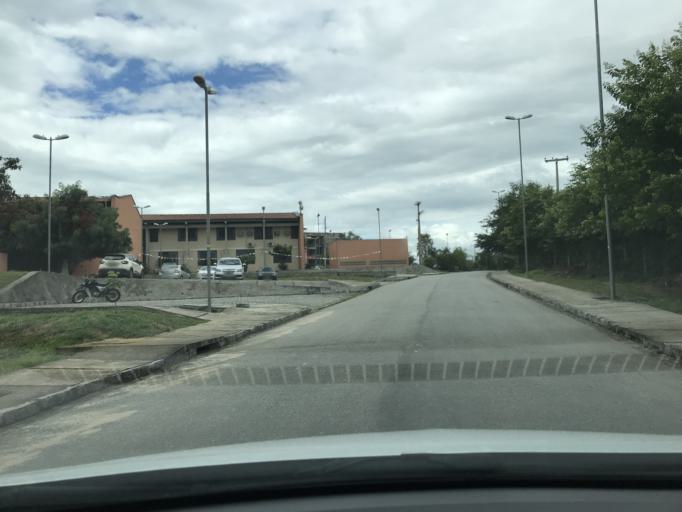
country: BR
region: Pernambuco
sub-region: Caruaru
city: Caruaru
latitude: -8.2254
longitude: -35.9828
